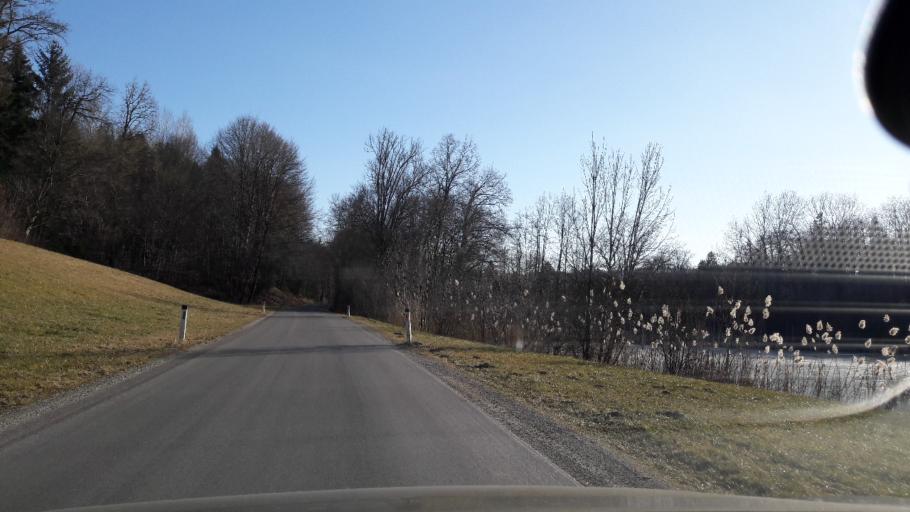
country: AT
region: Styria
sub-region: Politischer Bezirk Graz-Umgebung
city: Eisbach
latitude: 47.1121
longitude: 15.2739
